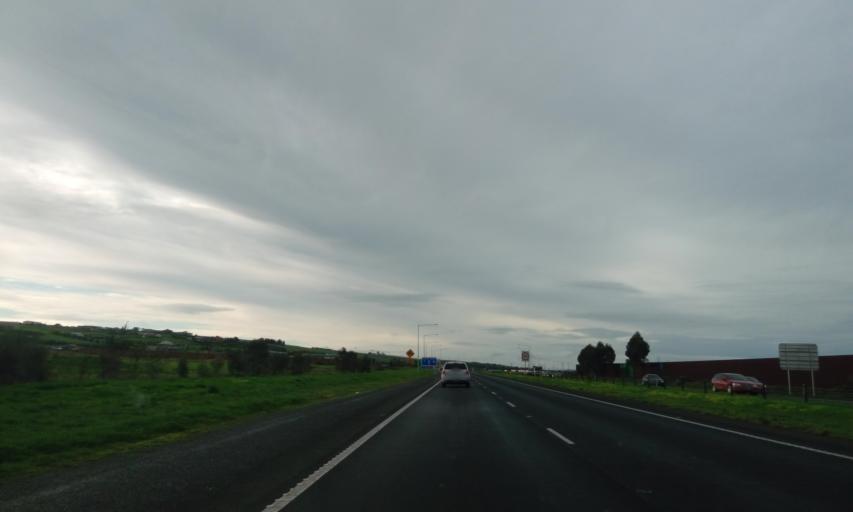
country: AU
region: Victoria
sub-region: Greater Geelong
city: Bell Post Hill
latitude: -38.0705
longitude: 144.3359
